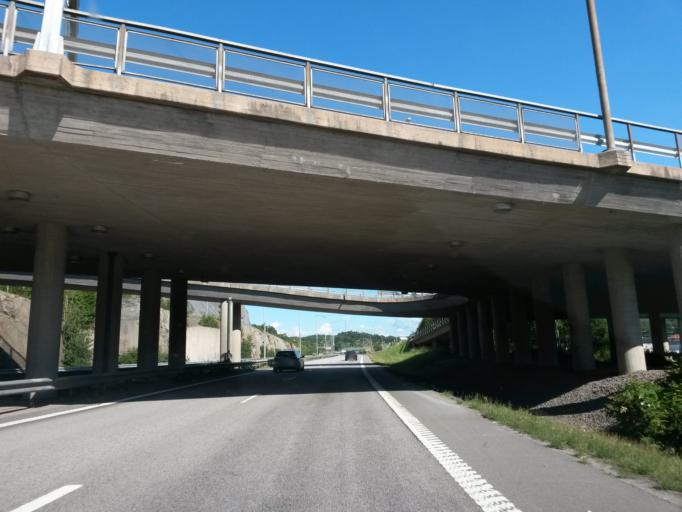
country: SE
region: Vaestra Goetaland
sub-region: Uddevalla Kommun
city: Uddevalla
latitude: 58.3562
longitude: 11.9117
